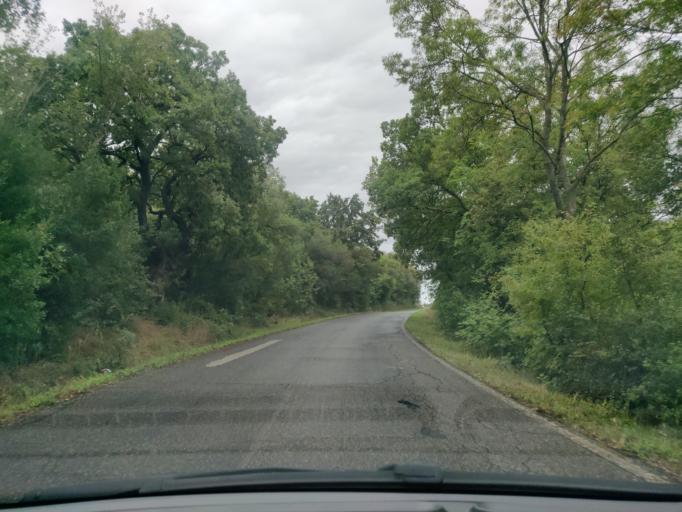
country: IT
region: Latium
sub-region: Citta metropolitana di Roma Capitale
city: Allumiere
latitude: 42.1280
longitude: 11.8559
